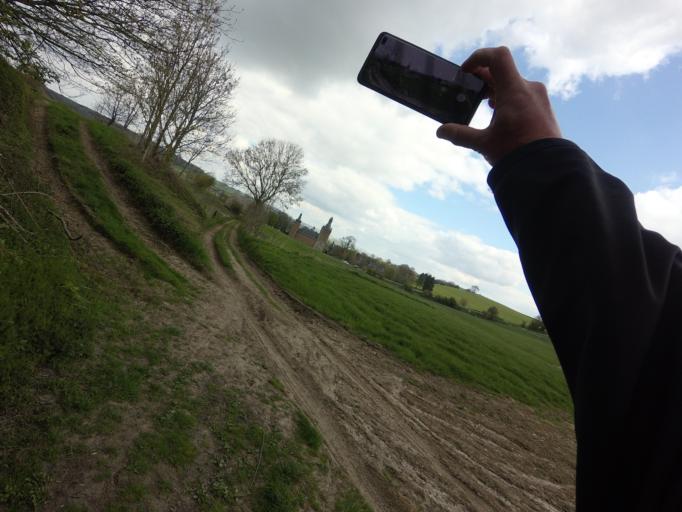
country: BE
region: Wallonia
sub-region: Province de Liege
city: Plombieres
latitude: 50.7483
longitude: 5.9102
